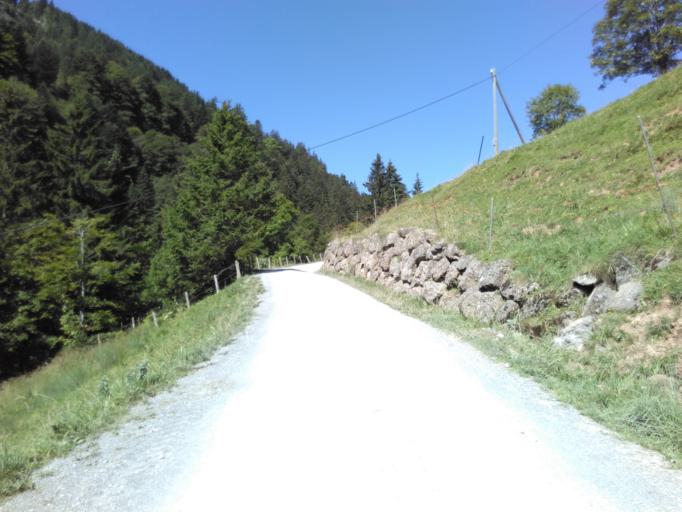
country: CH
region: Lucerne
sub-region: Lucerne-Land District
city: Vitznau
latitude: 47.0393
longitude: 8.4938
